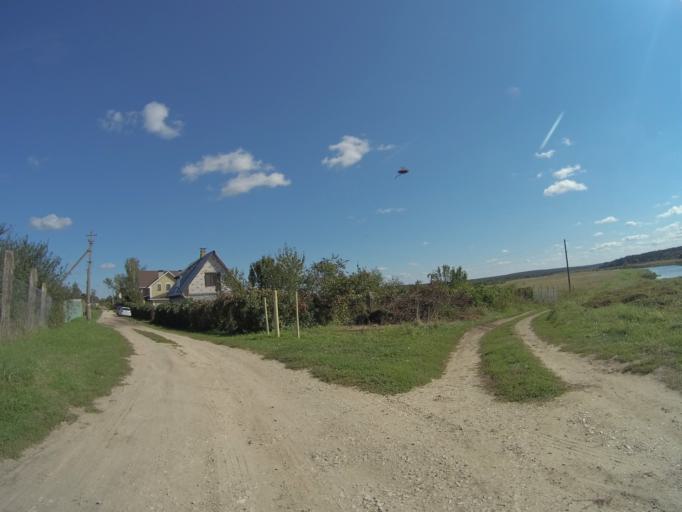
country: RU
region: Vladimir
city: Orgtrud
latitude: 56.3071
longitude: 40.6077
